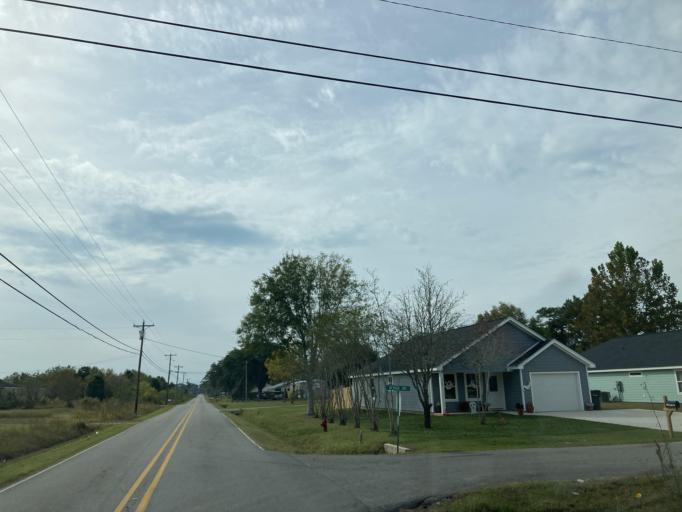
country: US
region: Mississippi
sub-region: Jackson County
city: Saint Martin
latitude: 30.4795
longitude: -88.8543
